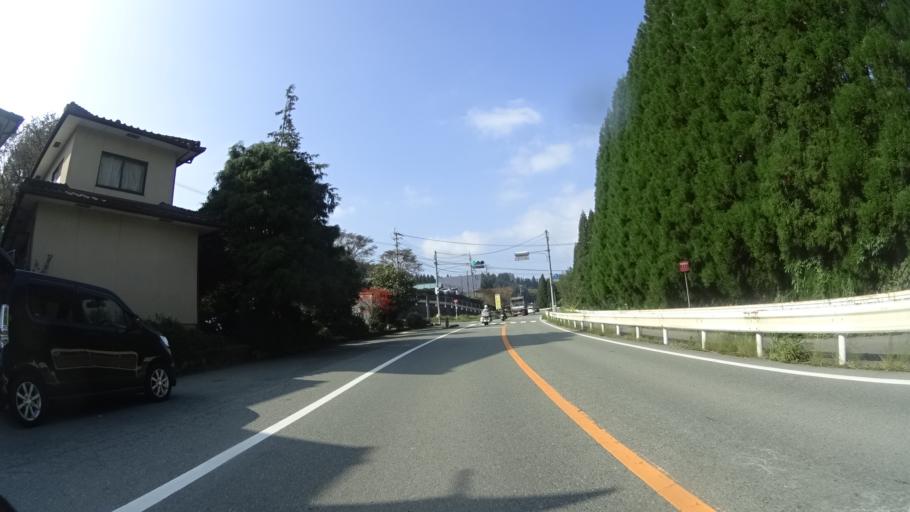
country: JP
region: Kumamoto
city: Aso
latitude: 33.1127
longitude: 131.0609
